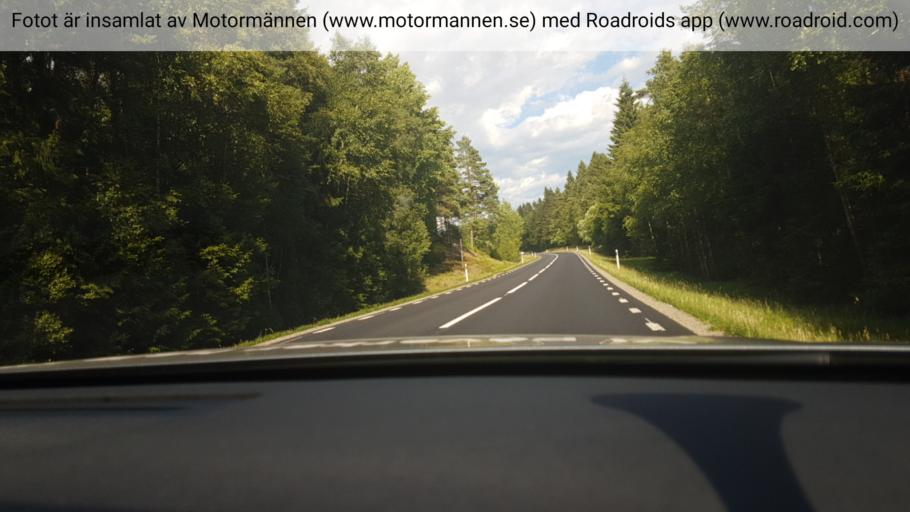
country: SE
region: Halland
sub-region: Hylte Kommun
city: Torup
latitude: 57.0954
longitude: 12.8403
